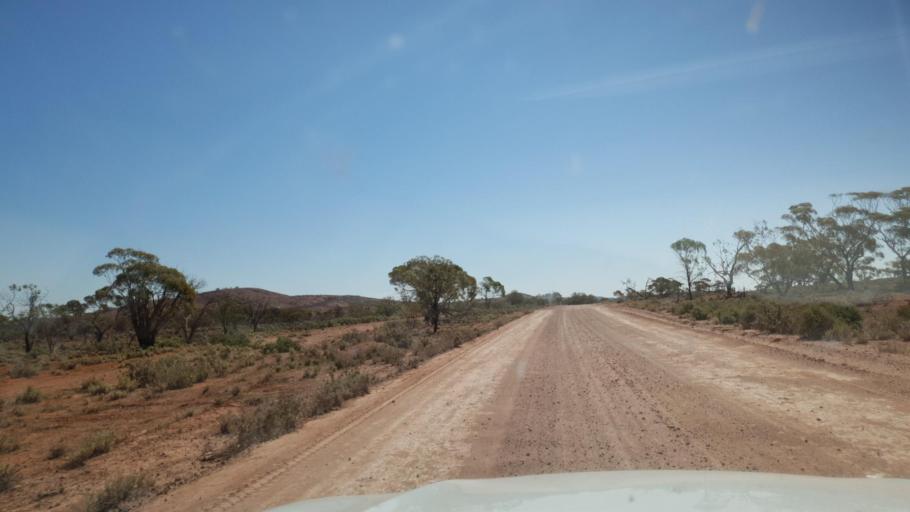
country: AU
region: South Australia
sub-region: Whyalla
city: Whyalla
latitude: -32.6126
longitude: 136.7522
